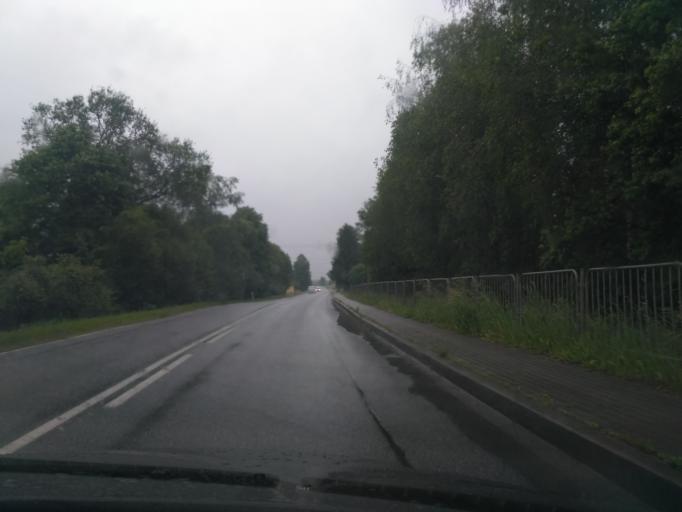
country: PL
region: Subcarpathian Voivodeship
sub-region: Powiat krosnienski
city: Leki
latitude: 49.8003
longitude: 21.6441
